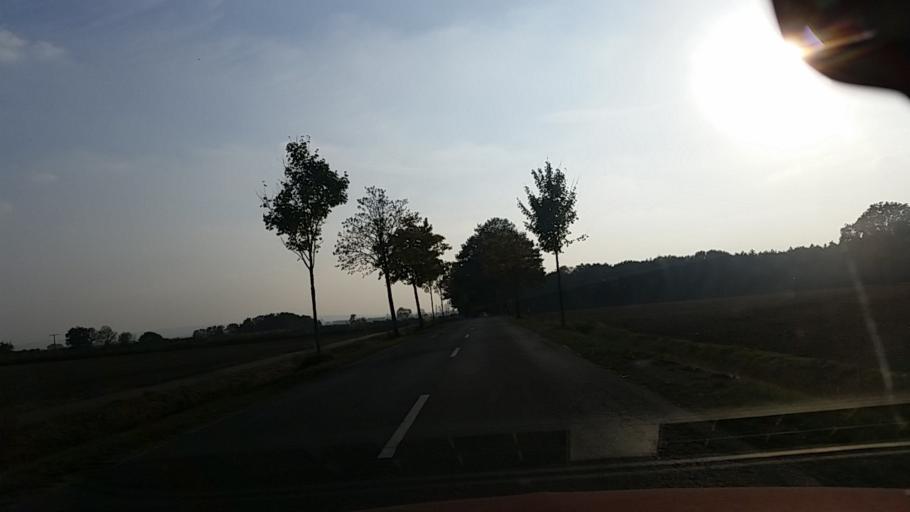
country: DE
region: Lower Saxony
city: Wolfsburg
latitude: 52.3752
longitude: 10.7983
